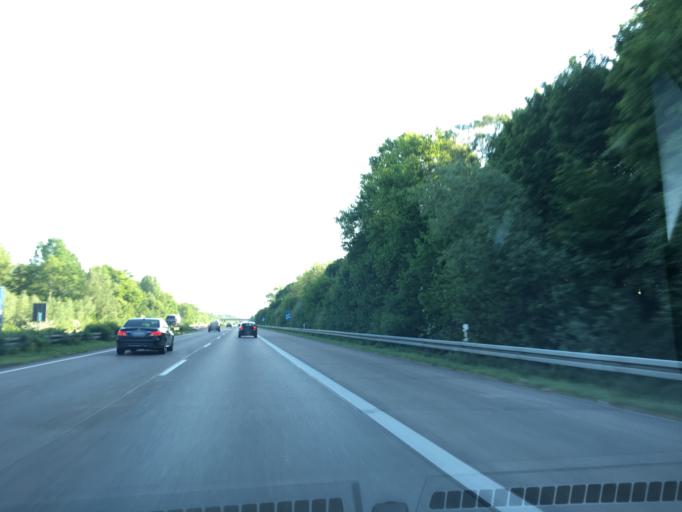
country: DE
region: North Rhine-Westphalia
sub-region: Regierungsbezirk Munster
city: Ladbergen
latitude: 52.1394
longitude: 7.7266
